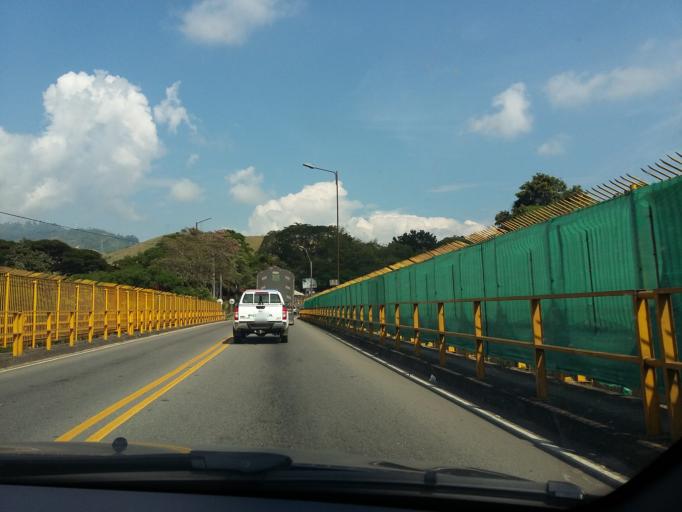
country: CO
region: Tolima
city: Ibague
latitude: 4.4055
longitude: -75.1823
